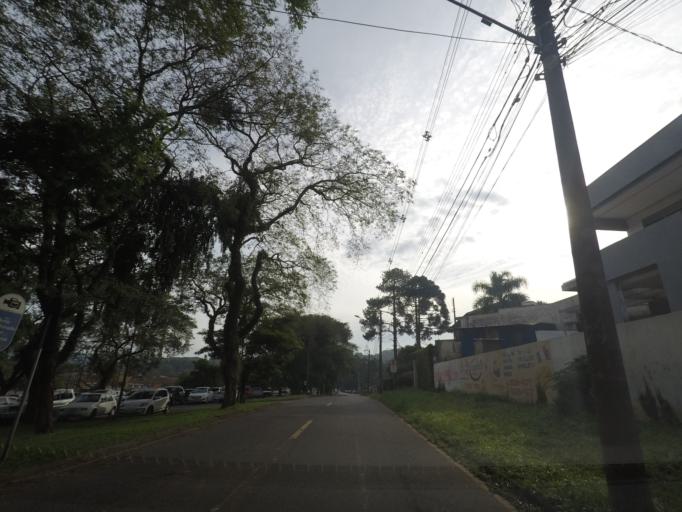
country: BR
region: Parana
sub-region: Curitiba
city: Curitiba
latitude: -25.4242
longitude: -49.3059
